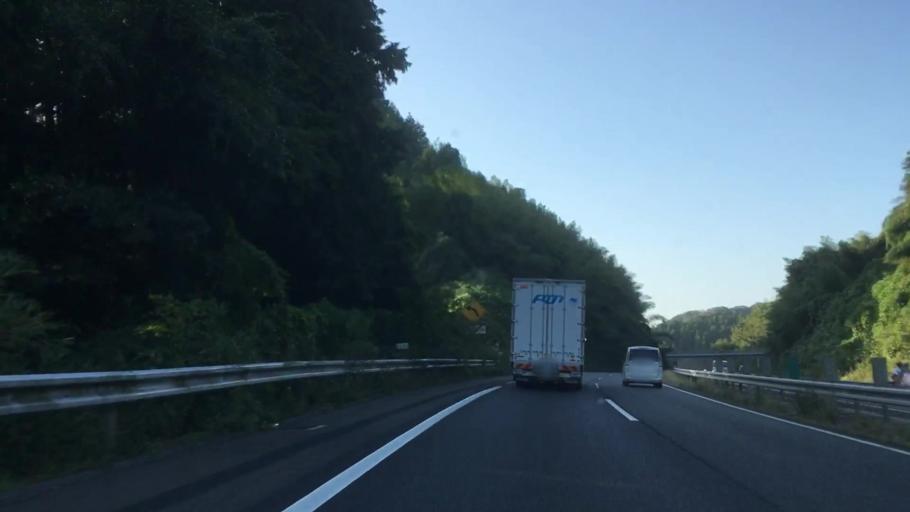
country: JP
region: Yamaguchi
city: Onoda
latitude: 34.1116
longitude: 131.1347
